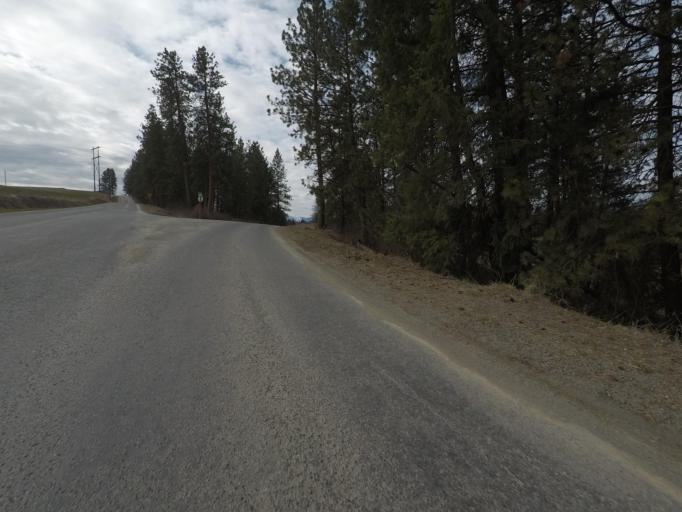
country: US
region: Washington
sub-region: Stevens County
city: Colville
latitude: 48.5288
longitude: -117.8796
